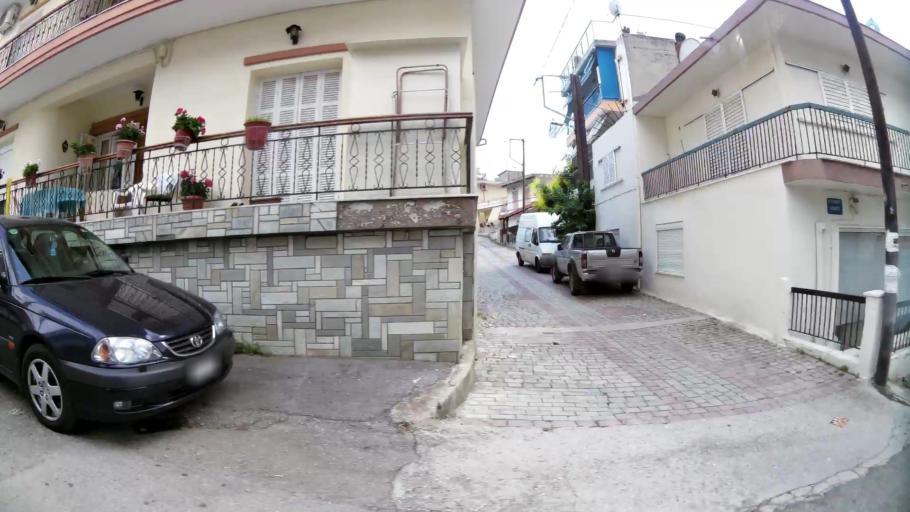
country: GR
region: Central Macedonia
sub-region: Nomos Thessalonikis
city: Stavroupoli
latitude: 40.6696
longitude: 22.9404
